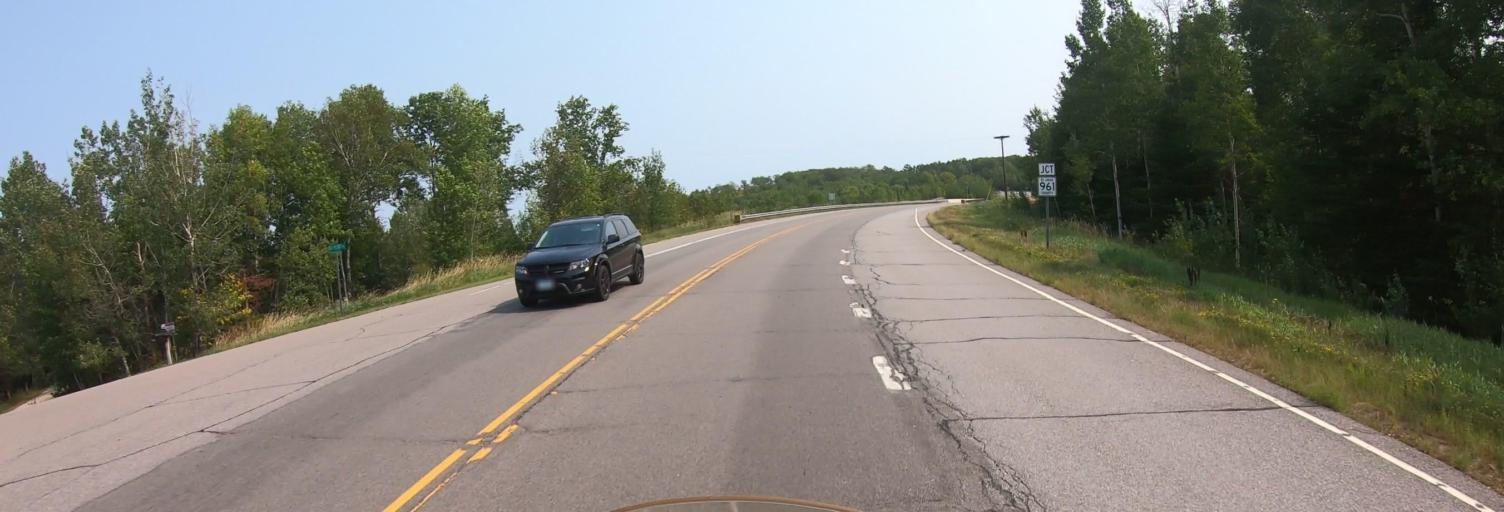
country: US
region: Minnesota
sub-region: Saint Louis County
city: Mountain Iron
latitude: 48.0635
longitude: -92.8297
